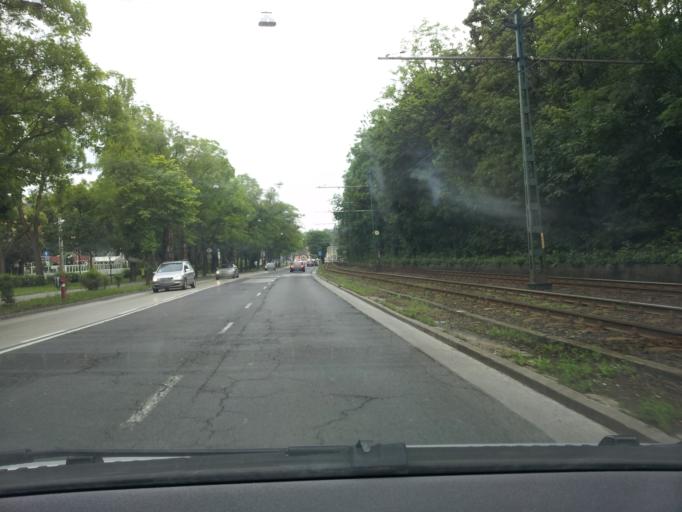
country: HU
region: Budapest
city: Budapest XII. keruelet
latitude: 47.5121
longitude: 19.0056
